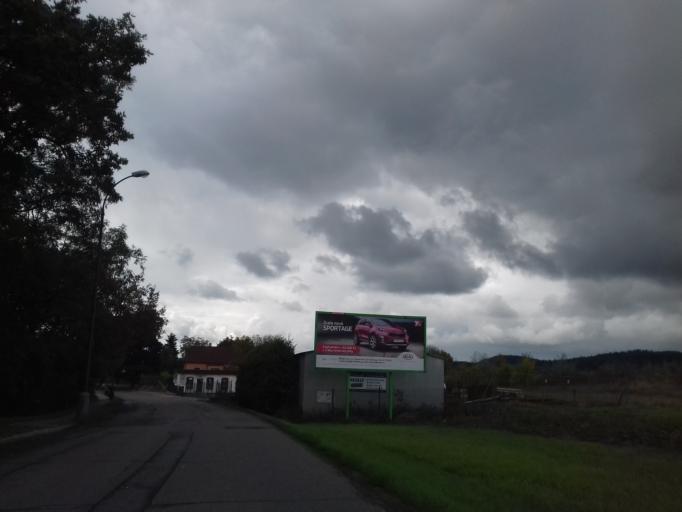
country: CZ
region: Central Bohemia
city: Vsenory
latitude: 49.9470
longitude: 14.3066
